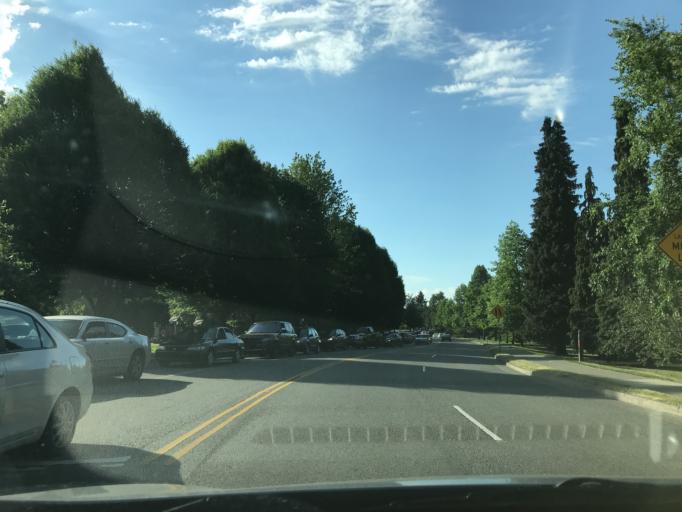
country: US
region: Washington
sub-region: King County
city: Issaquah
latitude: 47.5278
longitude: -122.0390
